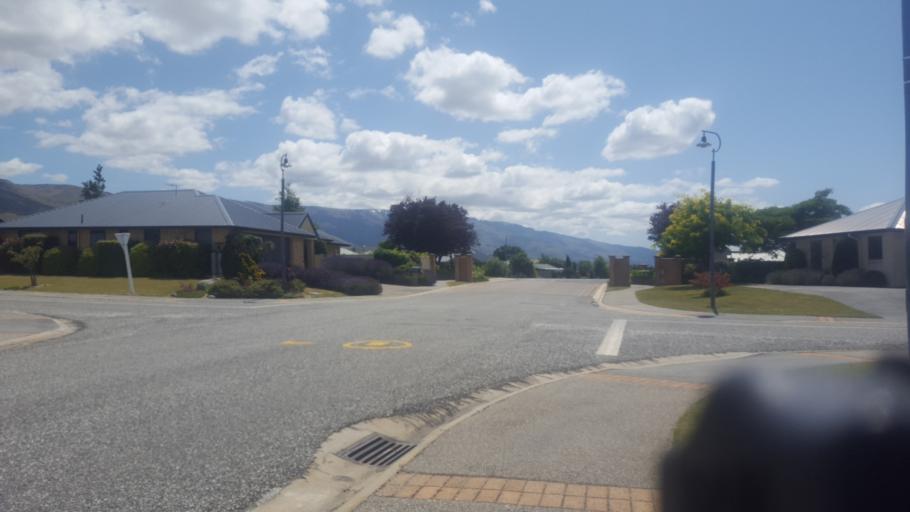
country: NZ
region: Otago
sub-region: Queenstown-Lakes District
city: Wanaka
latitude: -45.0486
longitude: 169.1992
